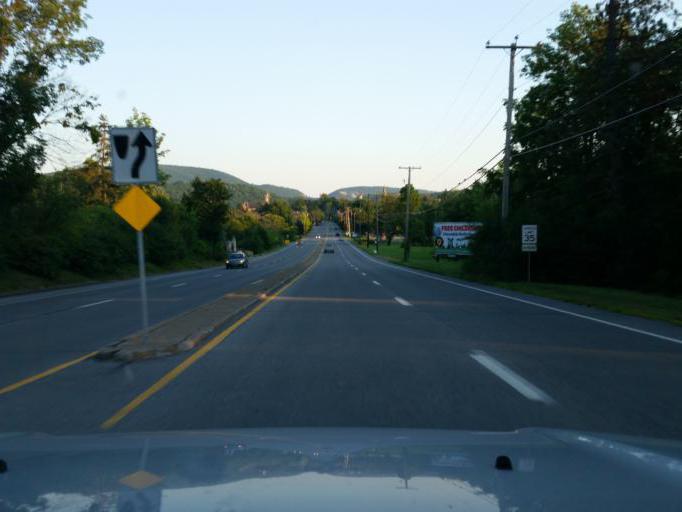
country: US
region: Pennsylvania
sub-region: Blair County
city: Hollidaysburg
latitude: 40.4416
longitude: -78.3929
